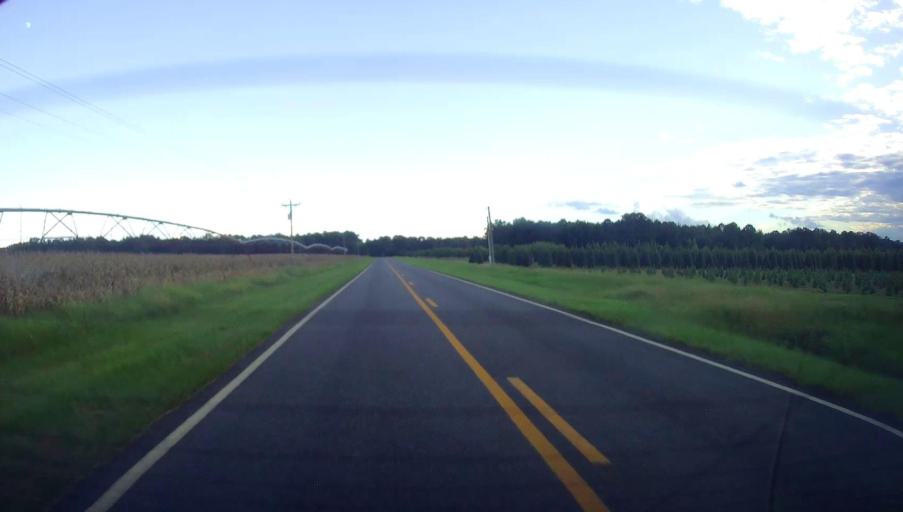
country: US
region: Georgia
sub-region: Pulaski County
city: Hawkinsville
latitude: 32.3027
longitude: -83.5529
